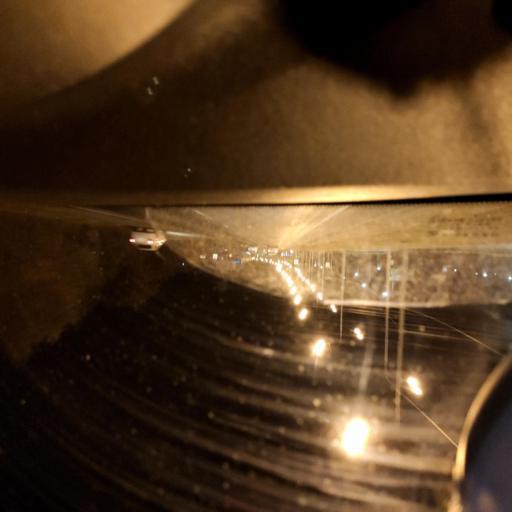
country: RU
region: Samara
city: Smyshlyayevka
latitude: 53.2624
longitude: 50.3828
